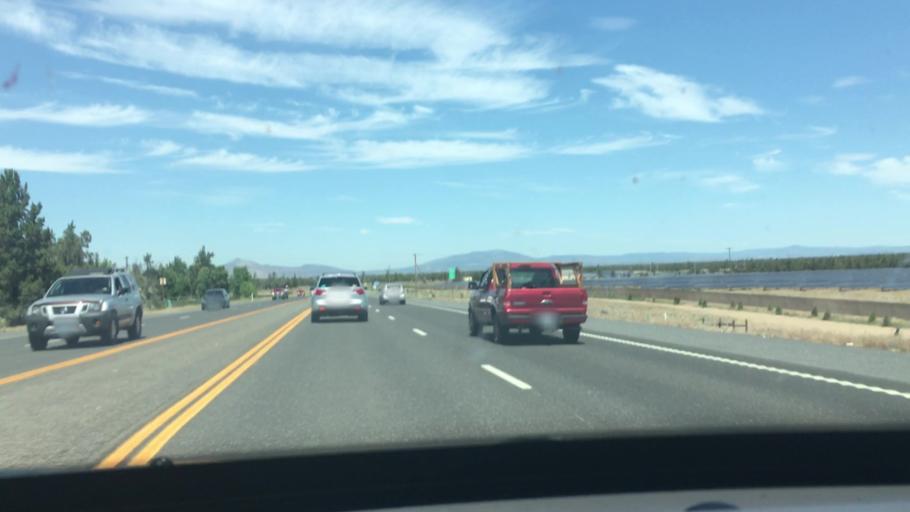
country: US
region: Oregon
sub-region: Deschutes County
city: Redmond
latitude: 44.1874
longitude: -121.2392
